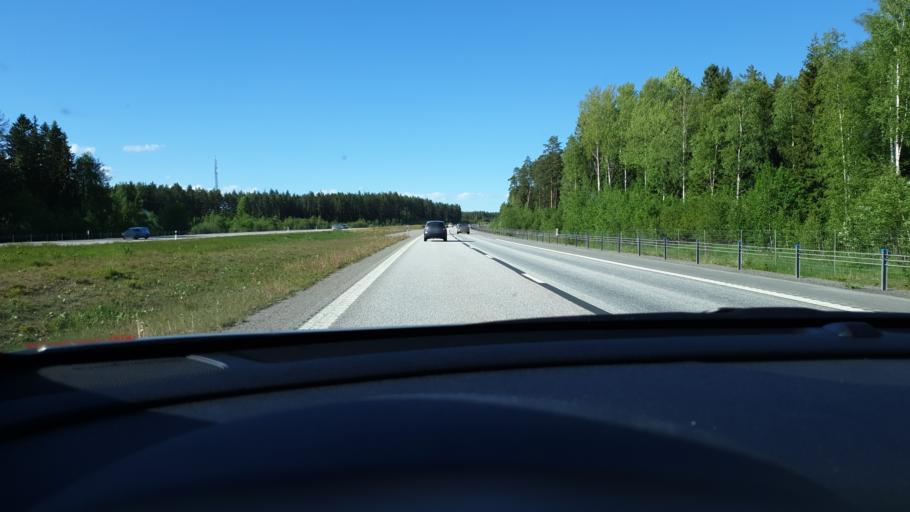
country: SE
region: Uppsala
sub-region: Tierps Kommun
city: Tierp
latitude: 60.2749
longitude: 17.5017
